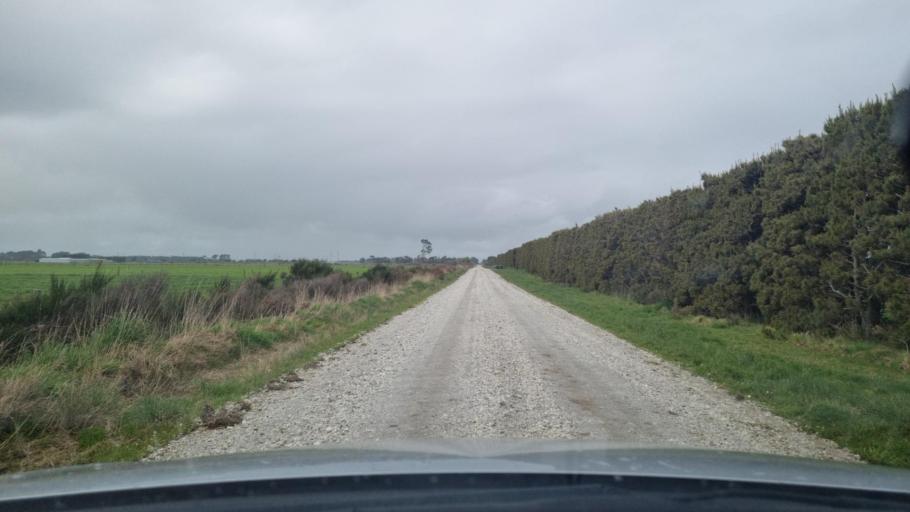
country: NZ
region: Southland
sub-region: Invercargill City
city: Invercargill
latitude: -46.5001
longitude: 168.4104
